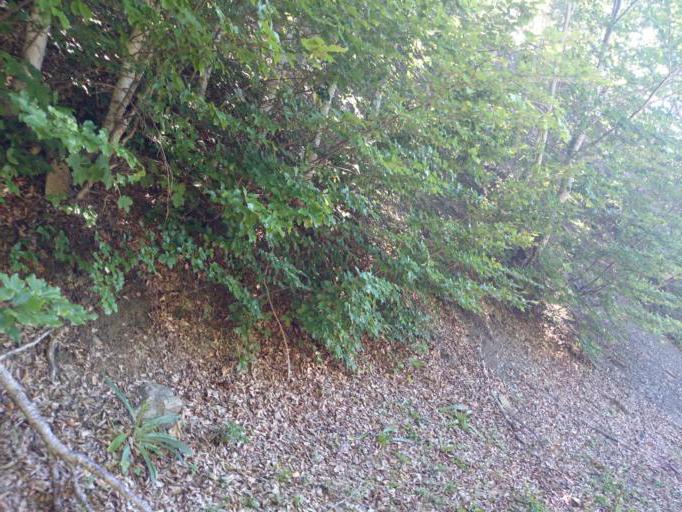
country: AL
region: Elbasan
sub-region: Rrethi i Gramshit
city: Kukur
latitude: 40.8517
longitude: 20.4140
